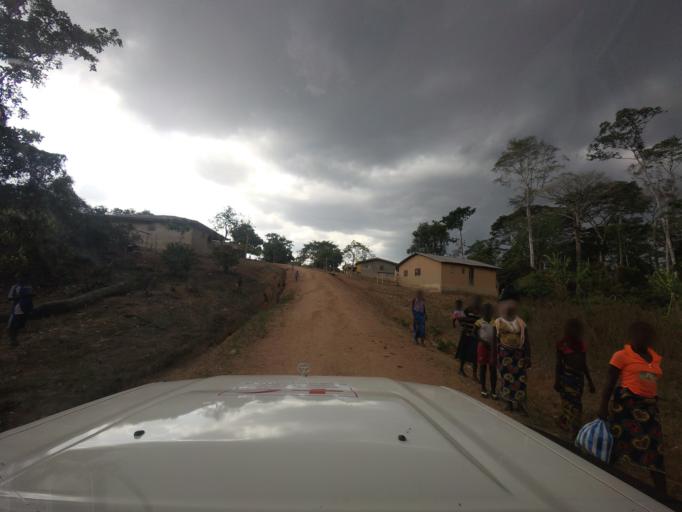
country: LR
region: Lofa
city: Voinjama
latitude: 8.4054
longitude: -9.6612
